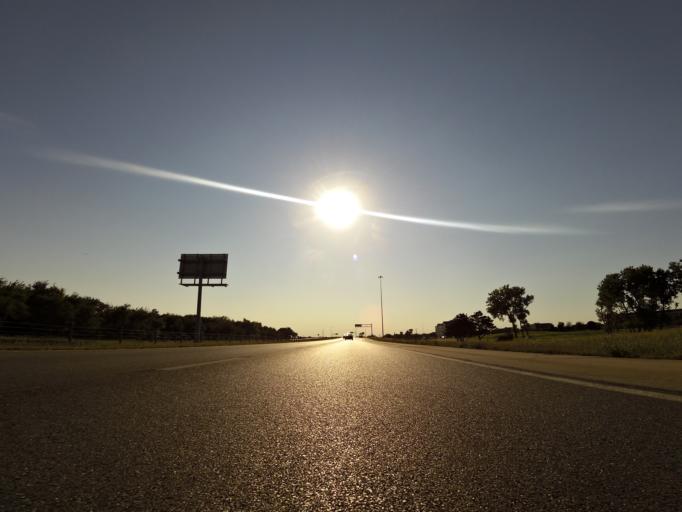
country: US
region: Kansas
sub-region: Sedgwick County
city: Bellaire
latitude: 37.7457
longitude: -97.2747
